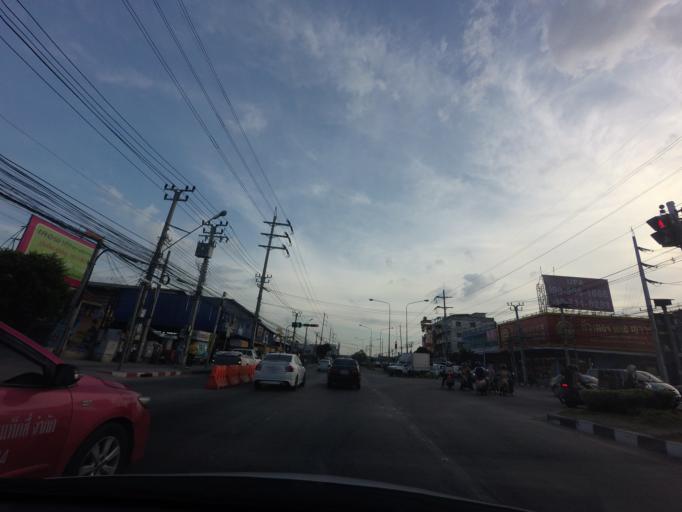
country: TH
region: Bangkok
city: Bang Khun Thian
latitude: 13.6299
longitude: 100.4342
